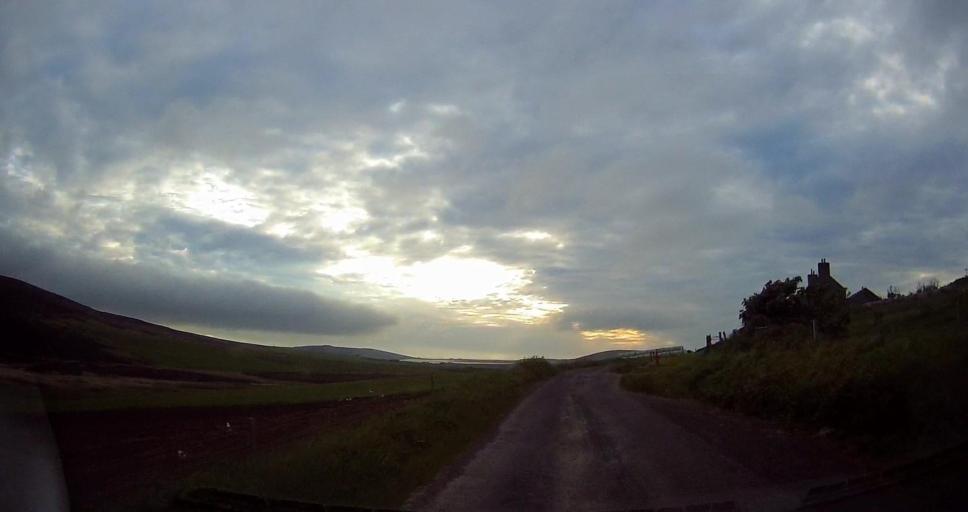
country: GB
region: Scotland
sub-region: Orkney Islands
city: Stromness
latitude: 59.1013
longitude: -3.2085
